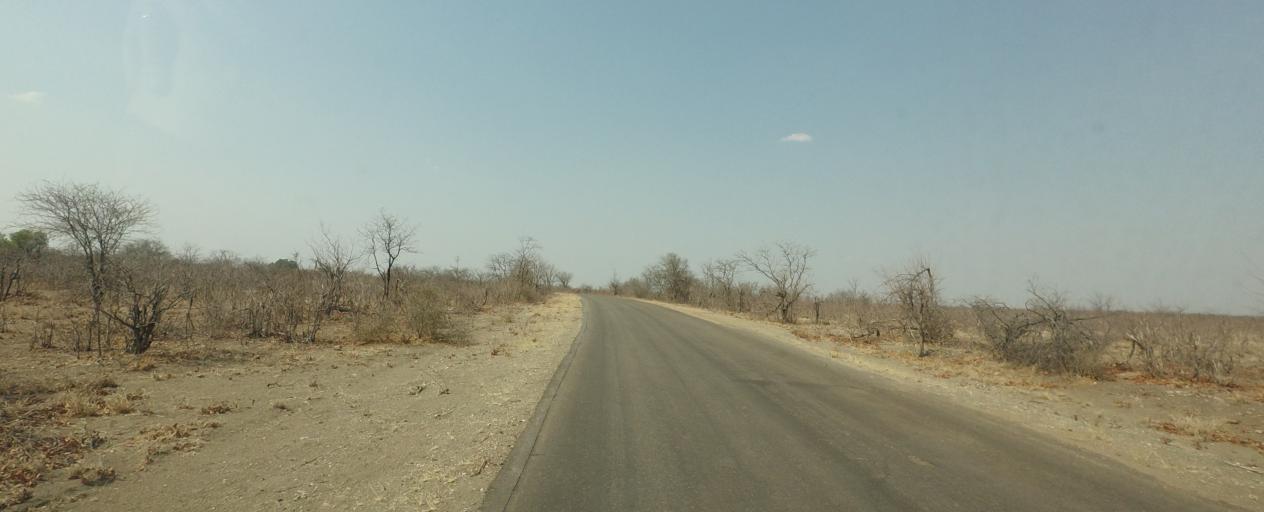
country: ZA
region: Limpopo
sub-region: Mopani District Municipality
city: Giyani
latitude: -23.1776
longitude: 31.3267
